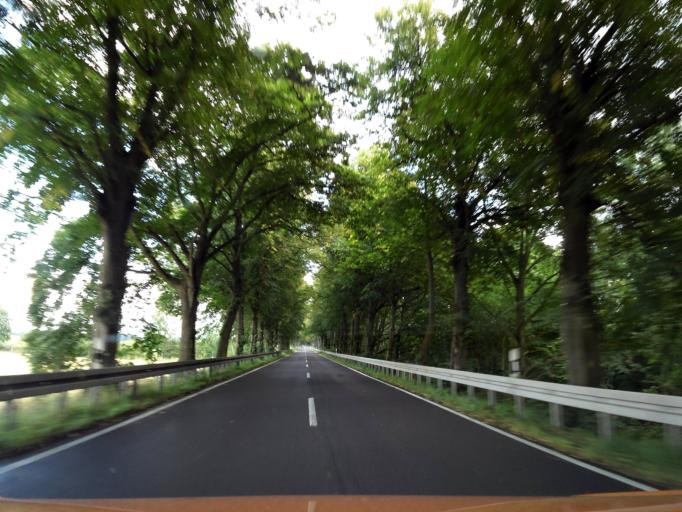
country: DE
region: Brandenburg
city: Wustermark
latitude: 52.4605
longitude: 12.9873
